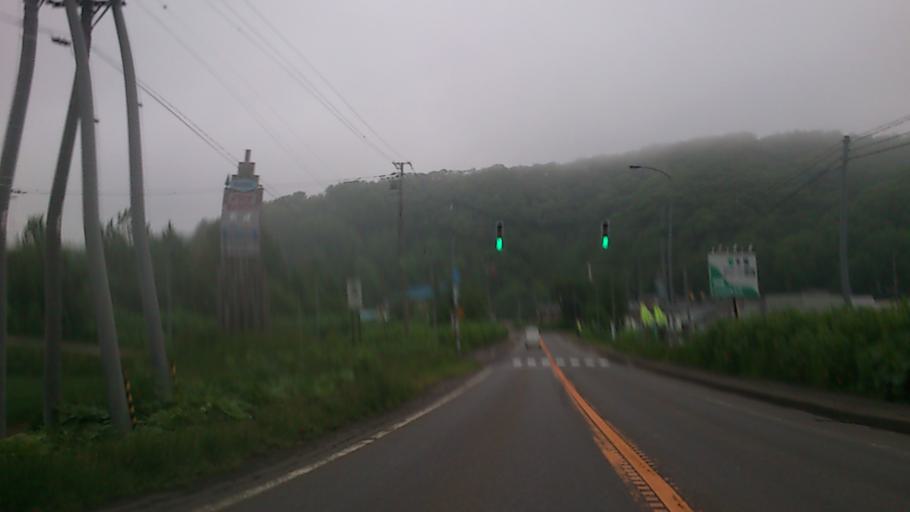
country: JP
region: Hokkaido
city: Niseko Town
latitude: 42.8288
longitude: 140.8908
